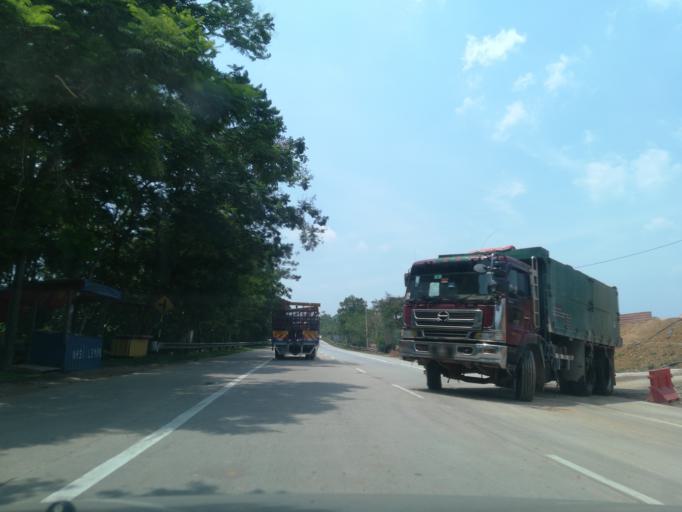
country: MY
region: Kedah
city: Kulim
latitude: 5.4263
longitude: 100.5642
